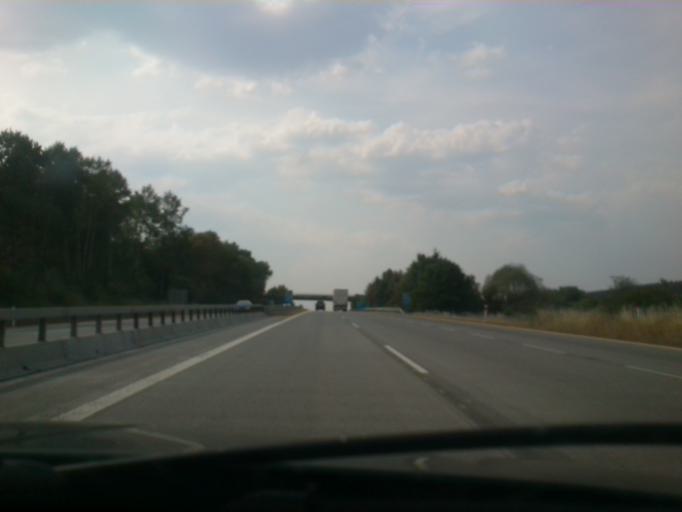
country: CZ
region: Central Bohemia
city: Divisov
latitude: 49.8007
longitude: 14.9102
